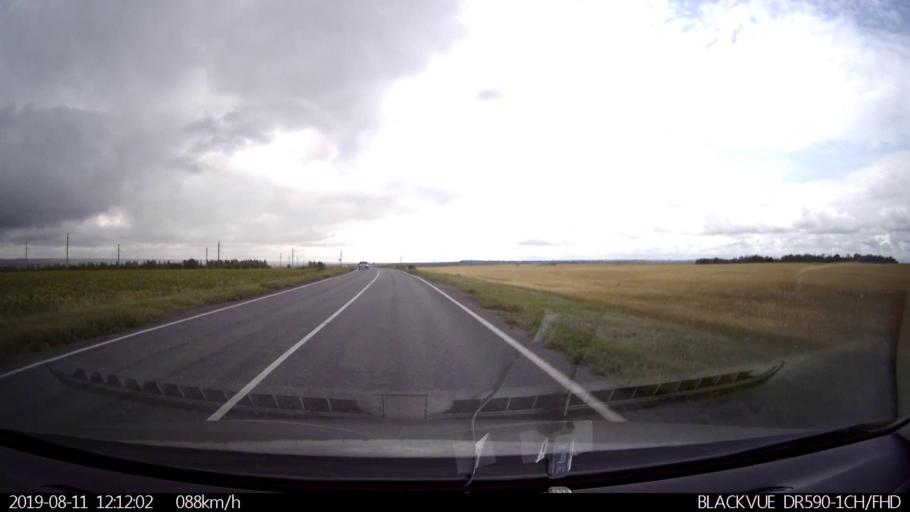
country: RU
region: Ulyanovsk
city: Silikatnyy
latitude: 53.9795
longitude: 47.9994
